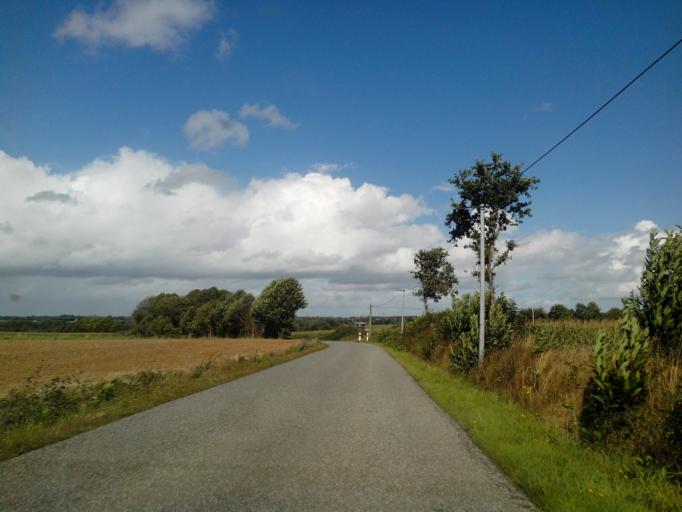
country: FR
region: Brittany
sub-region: Departement des Cotes-d'Armor
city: Merdrignac
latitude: 48.1640
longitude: -2.4182
